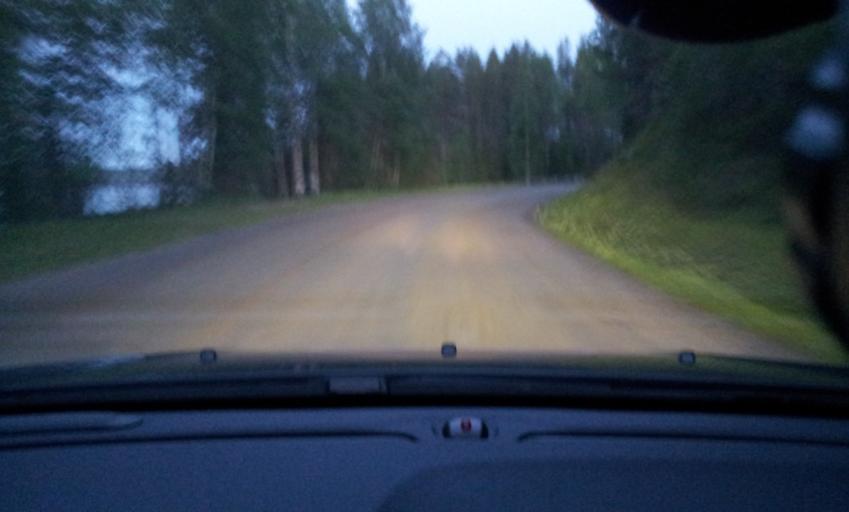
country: SE
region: Vaesternorrland
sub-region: Ange Kommun
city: Ange
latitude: 62.7227
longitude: 15.6373
